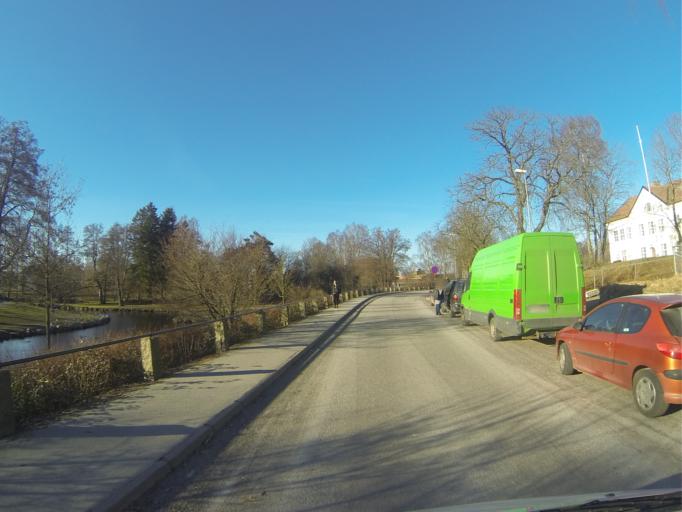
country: SE
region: Skane
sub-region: Hoors Kommun
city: Hoeoer
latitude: 55.9327
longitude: 13.5483
